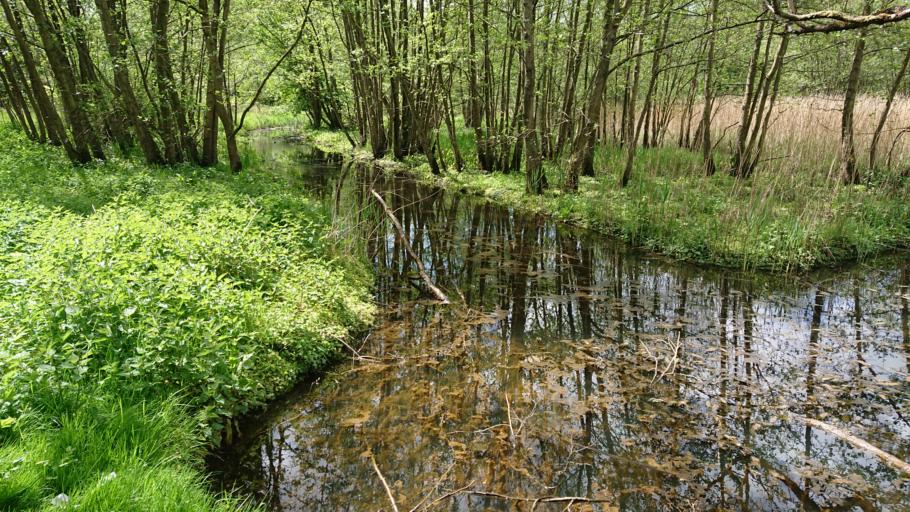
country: DK
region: Central Jutland
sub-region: Arhus Kommune
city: Stavtrup
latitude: 56.1719
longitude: 10.1136
